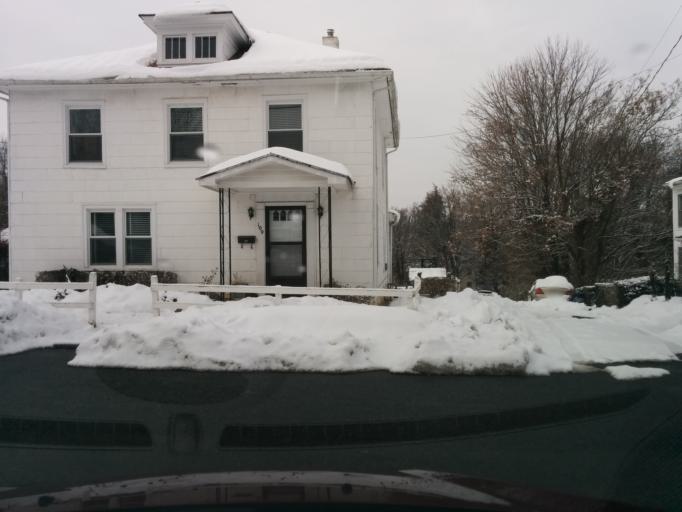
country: US
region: Virginia
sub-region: City of Lexington
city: Lexington
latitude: 37.7857
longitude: -79.4382
